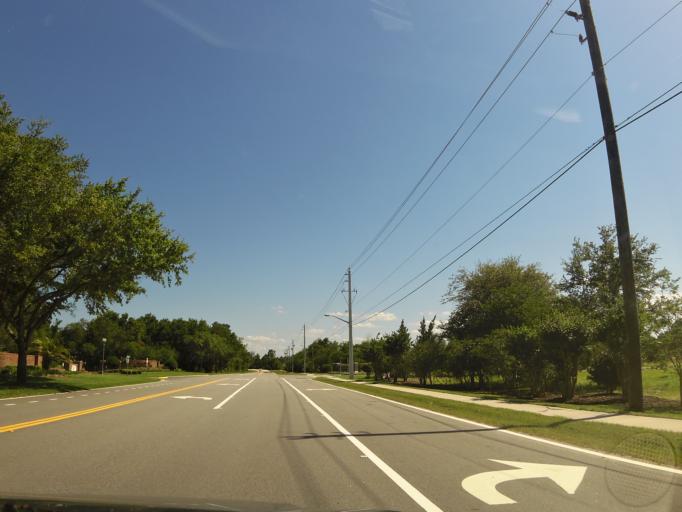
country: US
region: Florida
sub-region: Flagler County
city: Flagler Beach
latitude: 29.4113
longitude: -81.1482
